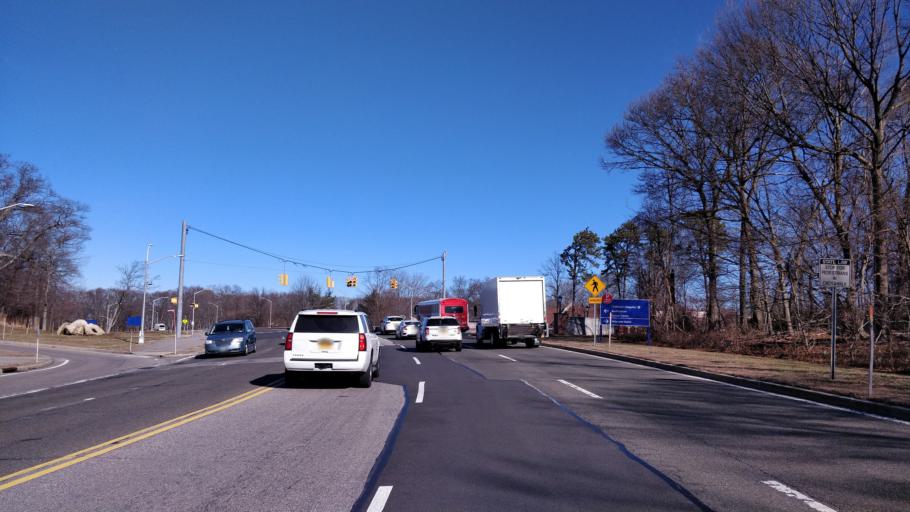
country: US
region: New York
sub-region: Suffolk County
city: Setauket-East Setauket
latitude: 40.9055
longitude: -73.1110
